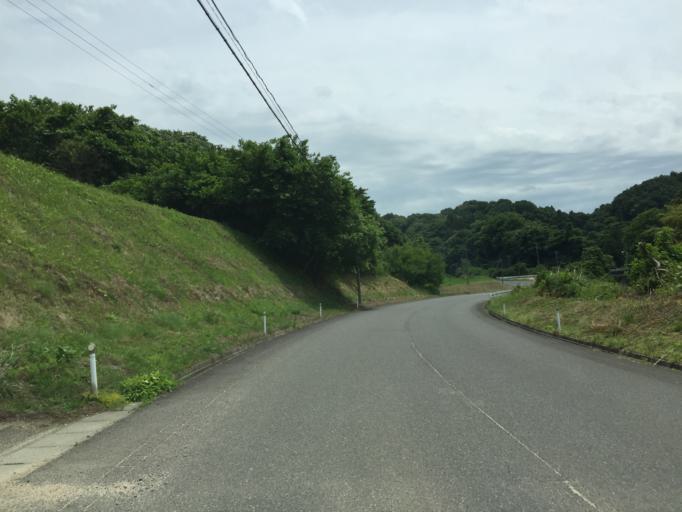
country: JP
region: Fukushima
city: Miharu
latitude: 37.4192
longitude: 140.5150
